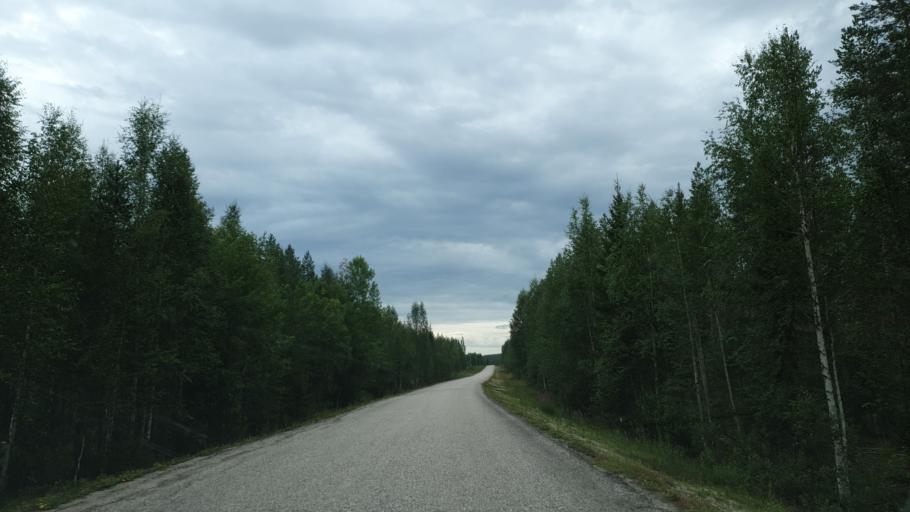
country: FI
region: Kainuu
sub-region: Kehys-Kainuu
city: Kuhmo
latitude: 64.3443
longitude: 29.2859
